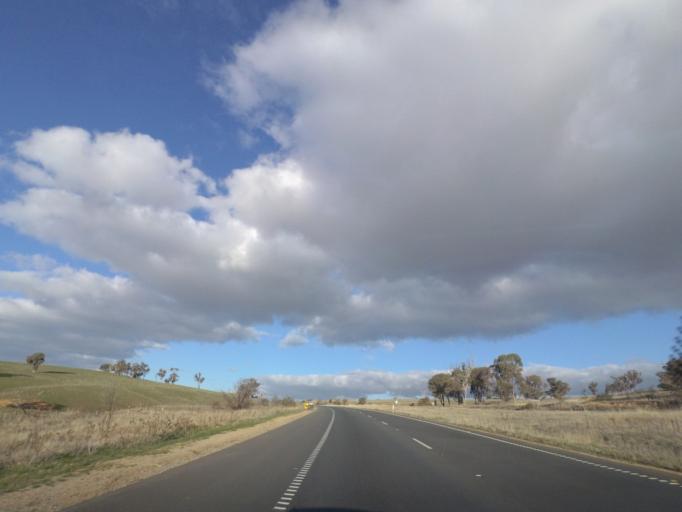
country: AU
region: New South Wales
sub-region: Gundagai
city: Gundagai
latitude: -34.8149
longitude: 148.4320
